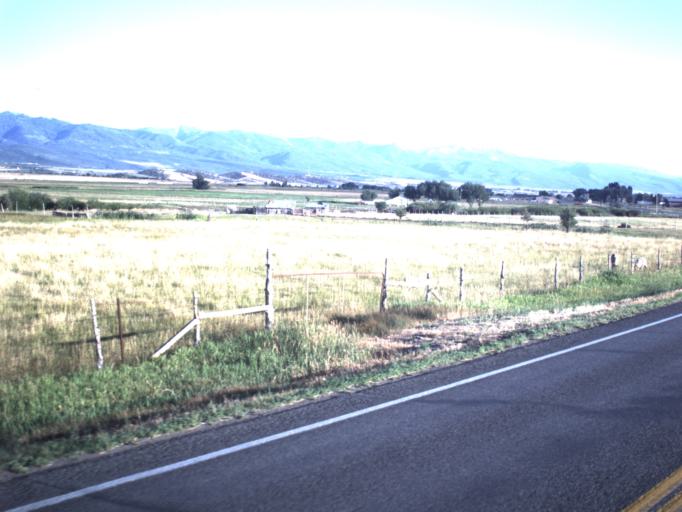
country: US
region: Utah
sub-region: Sanpete County
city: Fairview
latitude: 39.6153
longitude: -111.4437
